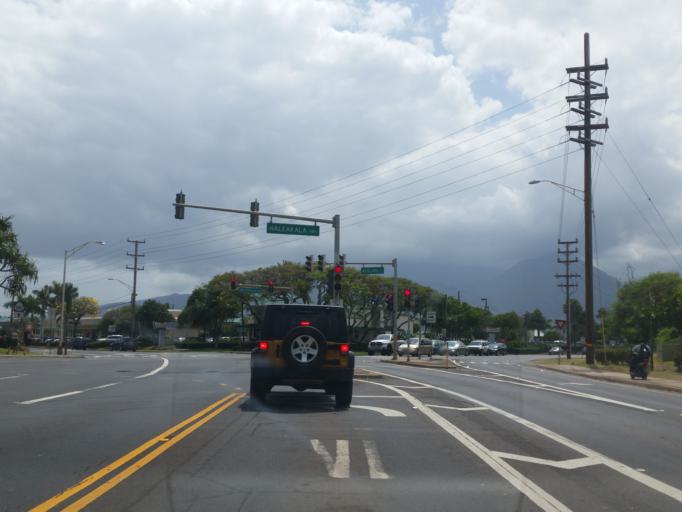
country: US
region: Hawaii
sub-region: Maui County
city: Kahului
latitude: 20.8881
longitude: -156.4514
